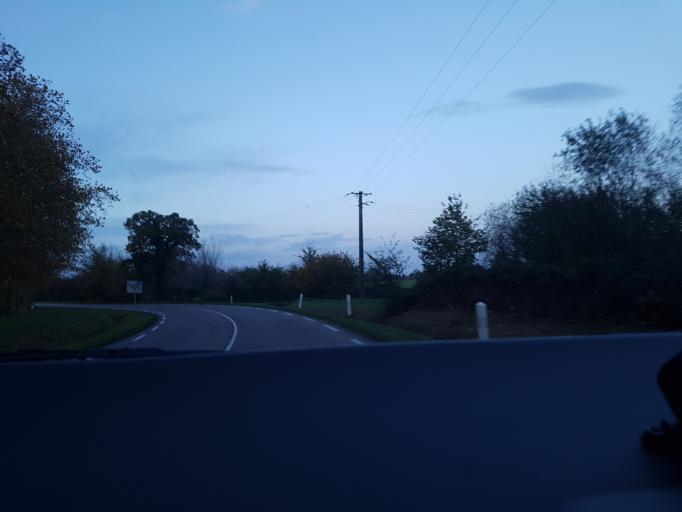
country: FR
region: Haute-Normandie
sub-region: Departement de l'Eure
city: Beuzeville
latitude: 49.3452
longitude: 0.3625
